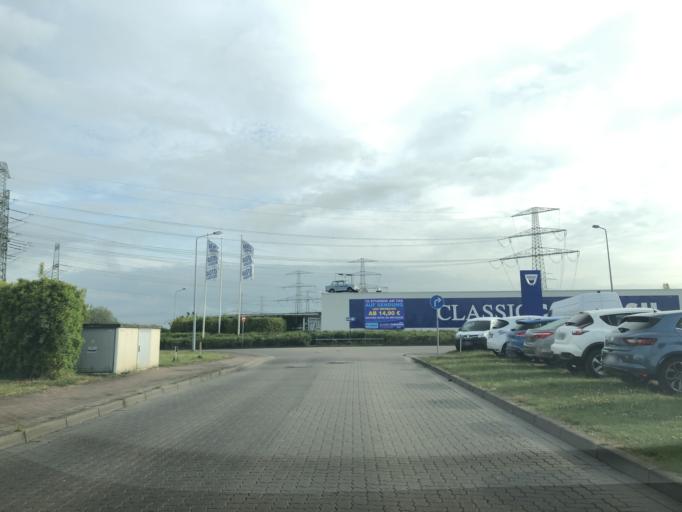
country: DE
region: Mecklenburg-Vorpommern
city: Guestrow
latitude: 53.8142
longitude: 12.1907
